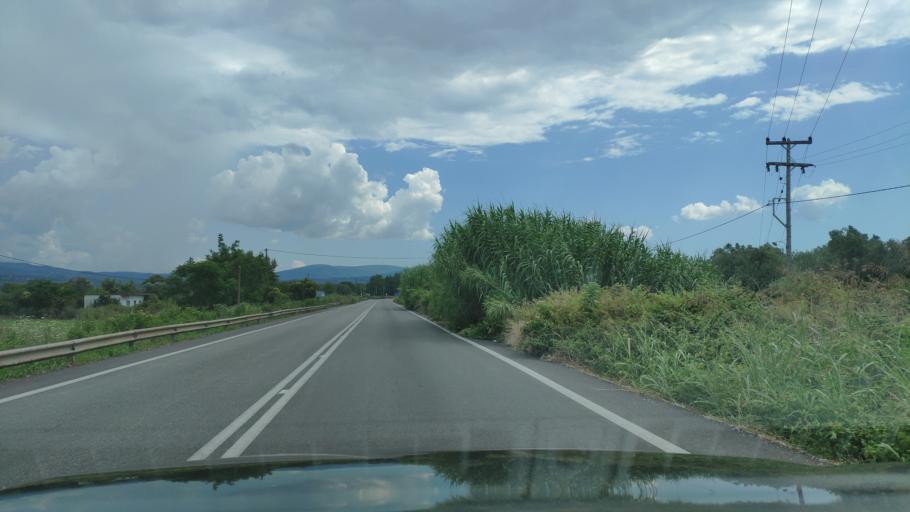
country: GR
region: West Greece
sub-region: Nomos Aitolias kai Akarnanias
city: Krikellos
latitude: 38.9223
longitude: 21.1781
